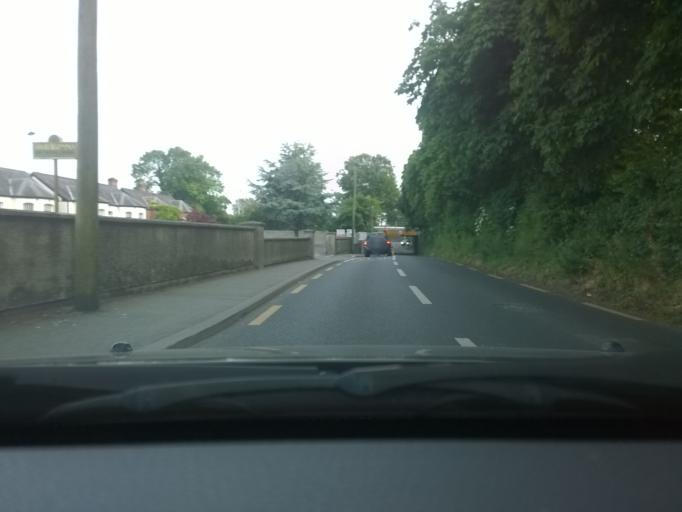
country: IE
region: Leinster
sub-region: Kildare
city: Kildare
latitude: 53.1629
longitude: -6.9121
